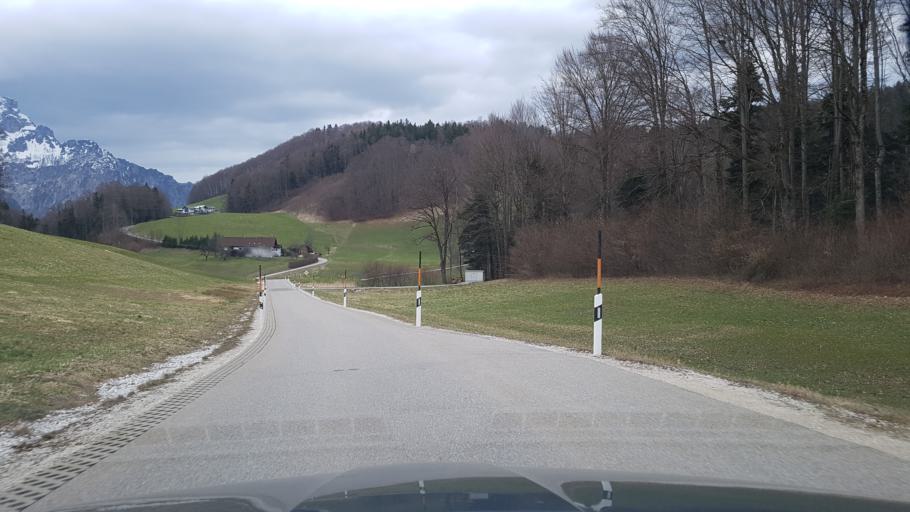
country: DE
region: Bavaria
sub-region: Upper Bavaria
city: Marktschellenberg
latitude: 47.6792
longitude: 13.0678
